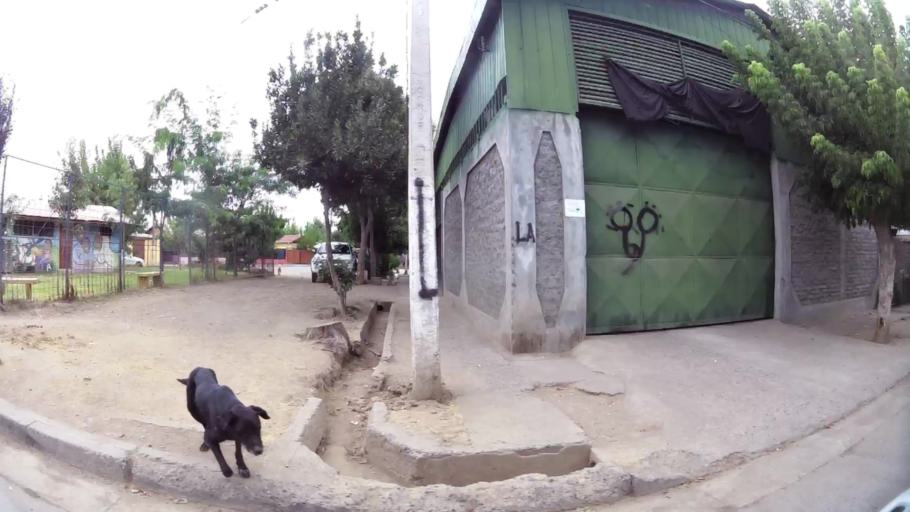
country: CL
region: O'Higgins
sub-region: Provincia de Cachapoal
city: Graneros
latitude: -34.0745
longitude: -70.7229
